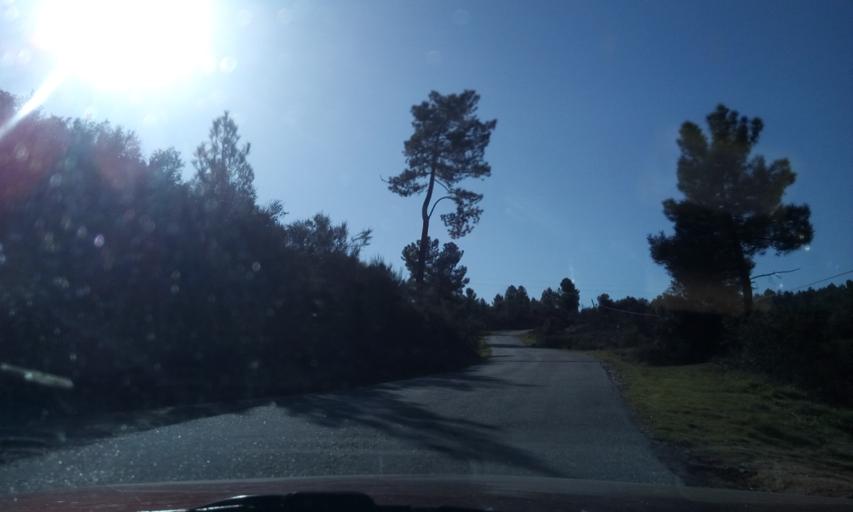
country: PT
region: Guarda
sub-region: Celorico da Beira
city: Celorico da Beira
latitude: 40.6833
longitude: -7.3973
